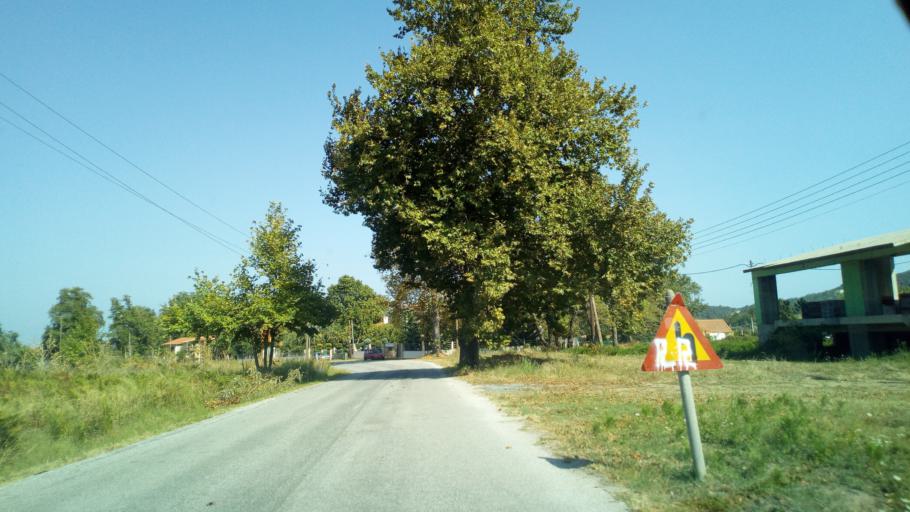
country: GR
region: Central Macedonia
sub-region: Nomos Chalkidikis
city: Stratonion
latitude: 40.5946
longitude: 23.7747
